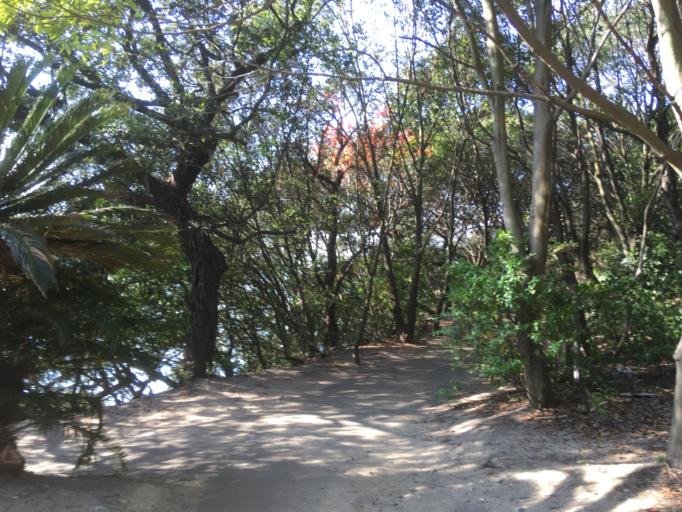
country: JP
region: Hiroshima
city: Fukuyama
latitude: 34.3840
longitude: 133.3896
